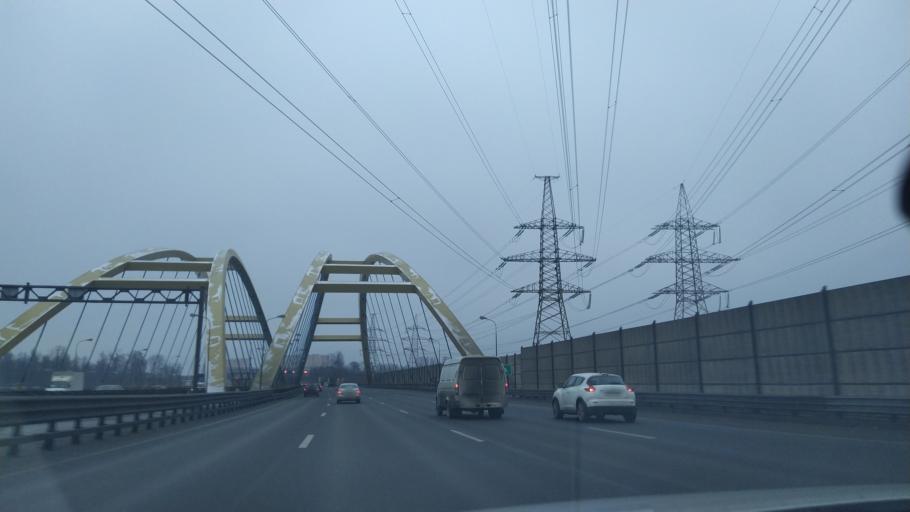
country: RU
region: St.-Petersburg
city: Krasnogvargeisky
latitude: 59.9861
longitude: 30.4910
